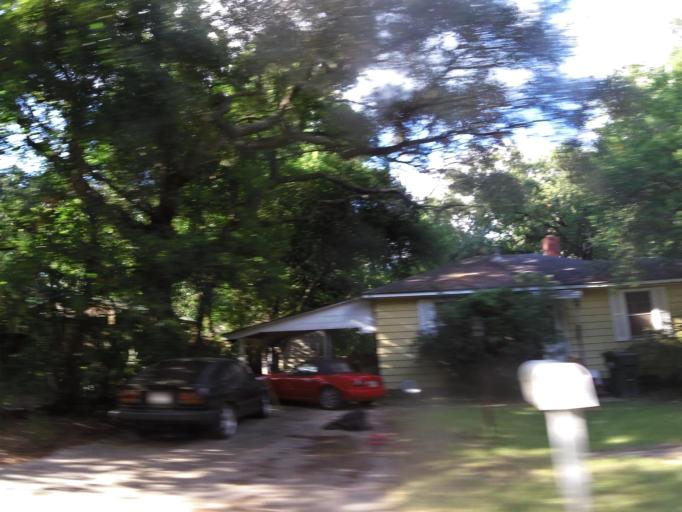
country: US
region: Georgia
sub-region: Glynn County
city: Saint Simons Island
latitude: 31.1685
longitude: -81.3801
